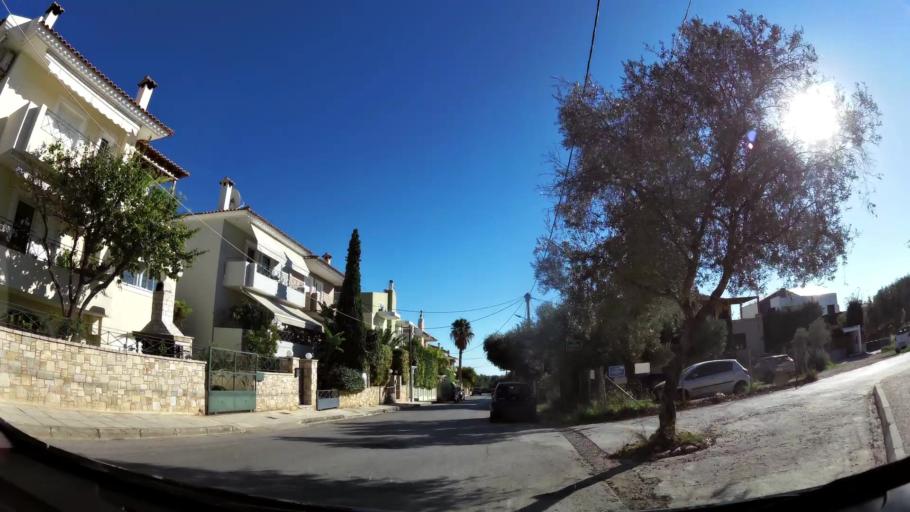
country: GR
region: Attica
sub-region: Nomarchia Anatolikis Attikis
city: Vari
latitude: 37.8347
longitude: 23.8139
